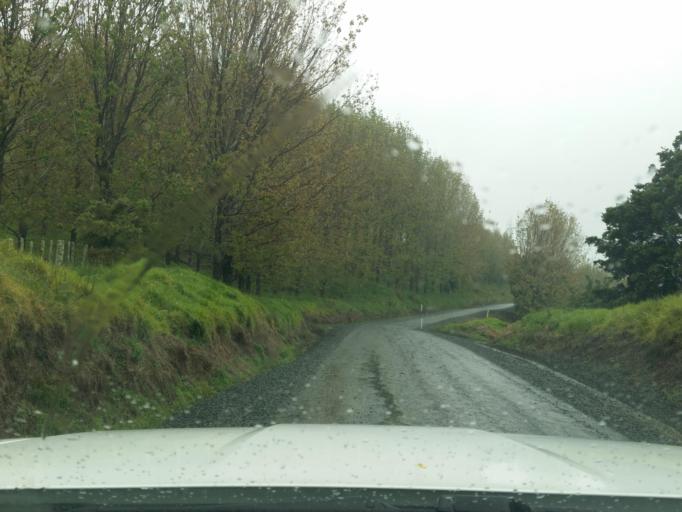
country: NZ
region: Northland
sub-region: Kaipara District
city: Dargaville
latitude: -35.7747
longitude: 173.9877
